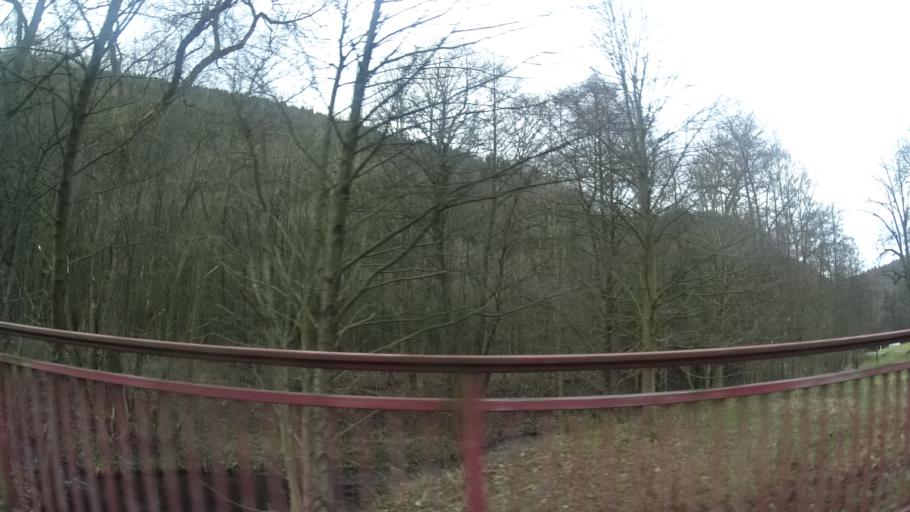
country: DE
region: Thuringia
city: Rohrbach
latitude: 50.6148
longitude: 11.2166
